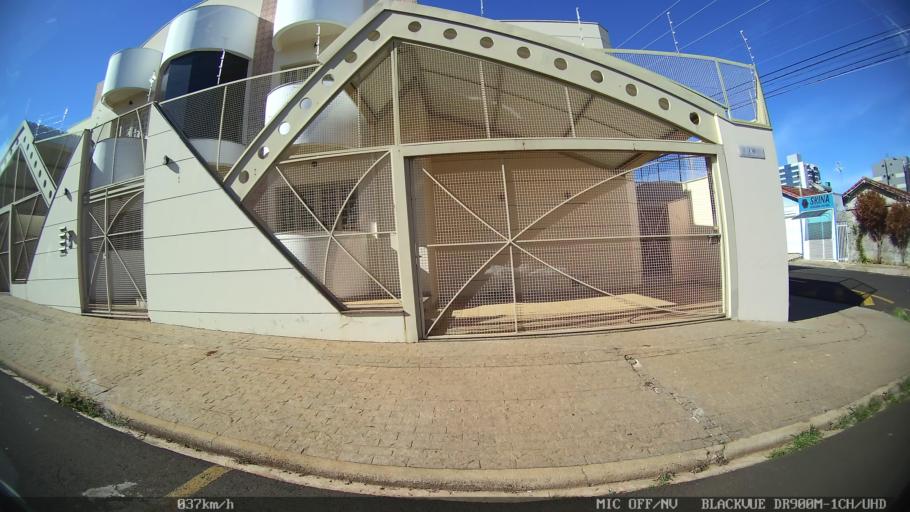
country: BR
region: Sao Paulo
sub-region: Franca
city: Franca
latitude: -20.5446
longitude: -47.3960
